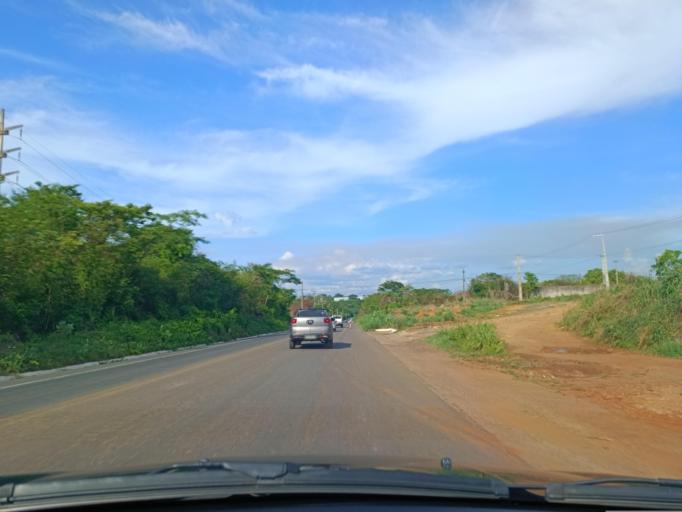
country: BR
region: Piaui
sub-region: Teresina
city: Teresina
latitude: -5.0884
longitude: -42.7589
